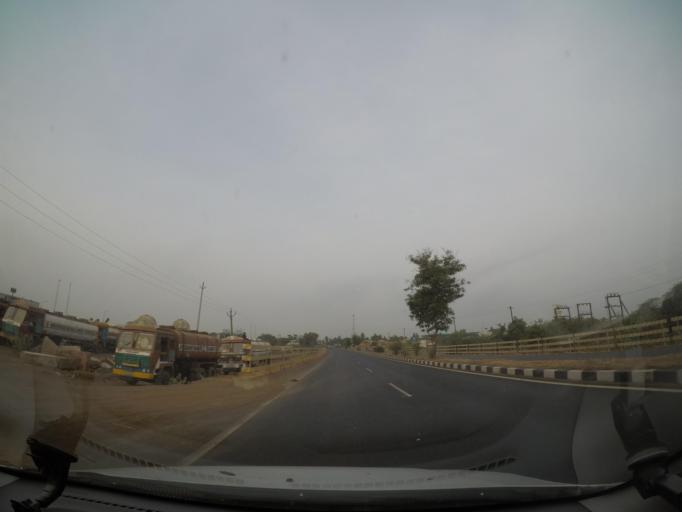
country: IN
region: Andhra Pradesh
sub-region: Krishna
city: Gannavaram
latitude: 16.6003
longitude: 80.8966
